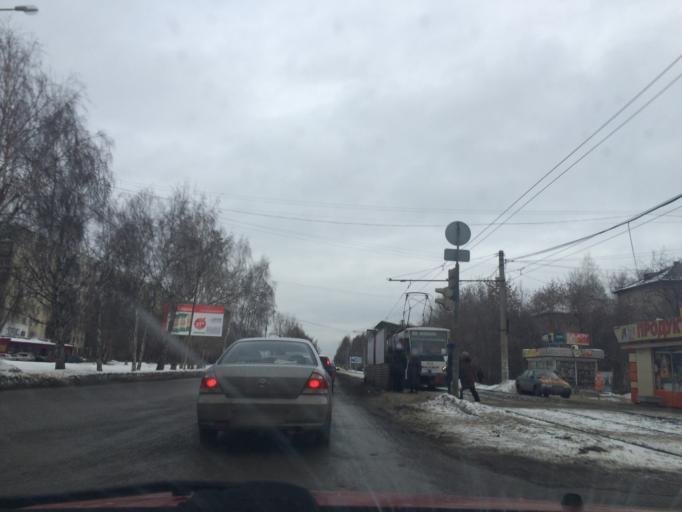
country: RU
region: Sverdlovsk
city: Yekaterinburg
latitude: 56.8534
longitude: 60.6456
